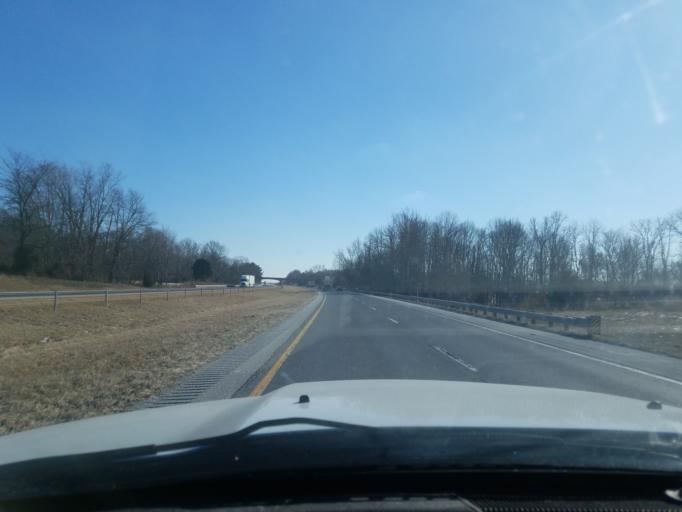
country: US
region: Indiana
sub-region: Jackson County
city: Seymour
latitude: 39.0069
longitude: -85.8667
